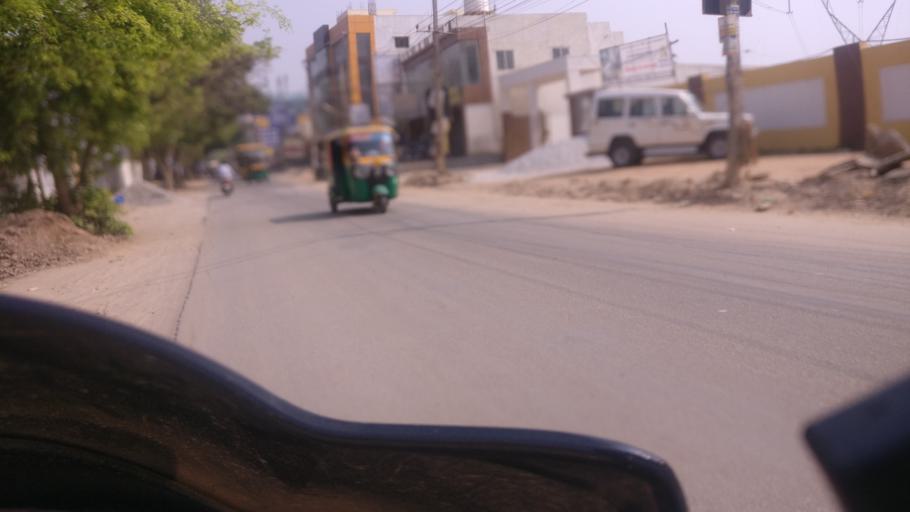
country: IN
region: Karnataka
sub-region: Bangalore Urban
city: Bangalore
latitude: 12.8782
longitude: 77.6718
